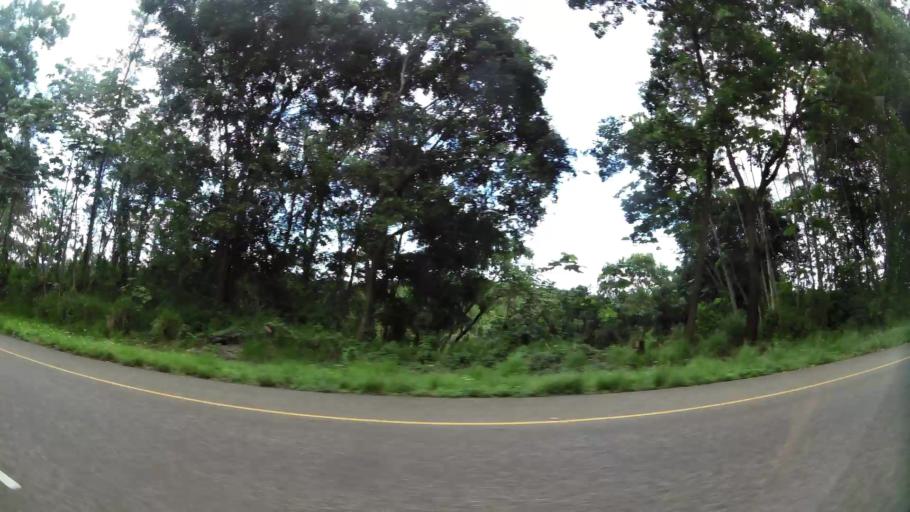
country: DO
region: La Vega
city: Rincon
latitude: 19.1048
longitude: -70.4434
